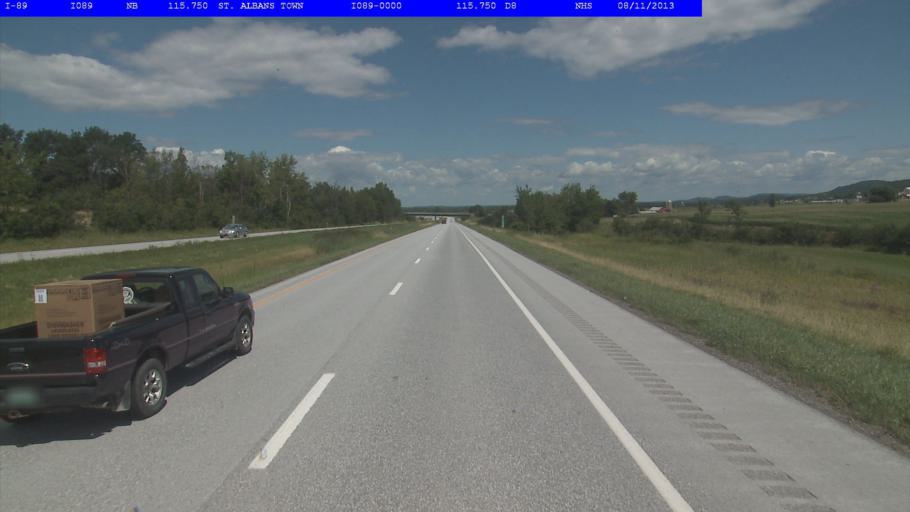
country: US
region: Vermont
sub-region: Franklin County
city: Saint Albans
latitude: 44.8231
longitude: -73.0624
